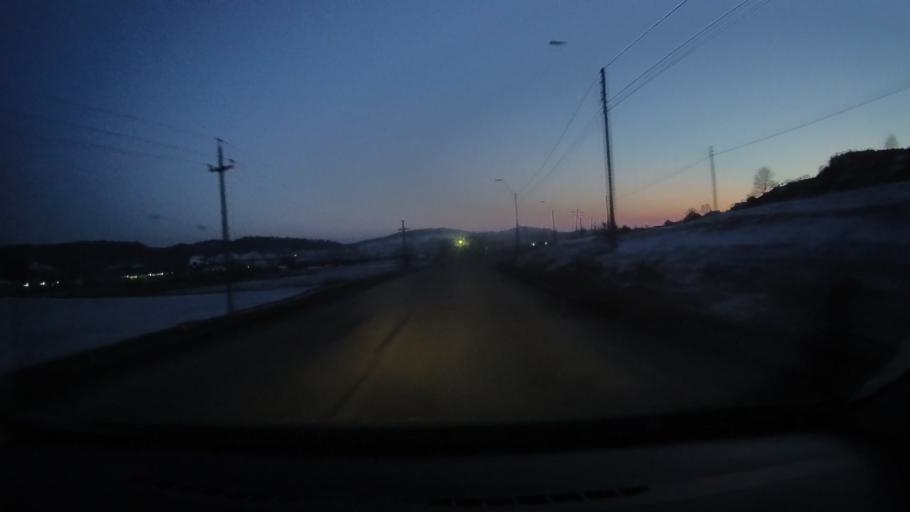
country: RO
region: Sibiu
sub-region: Municipiul Medias
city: Medias
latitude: 46.1807
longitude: 24.3691
